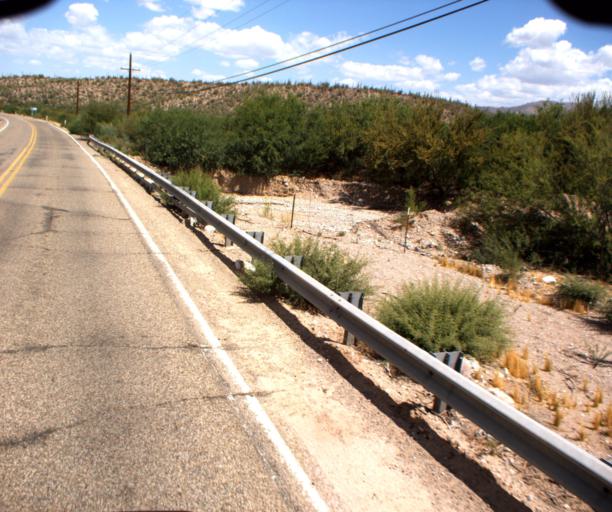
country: US
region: Arizona
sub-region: Pinal County
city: Kearny
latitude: 33.0488
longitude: -110.8899
